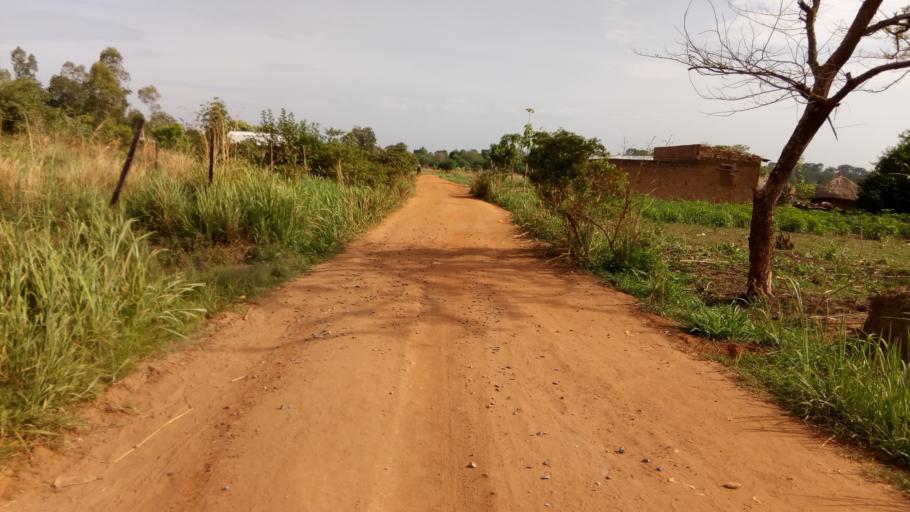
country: UG
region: Northern Region
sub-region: Gulu District
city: Gulu
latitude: 2.7978
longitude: 32.3236
